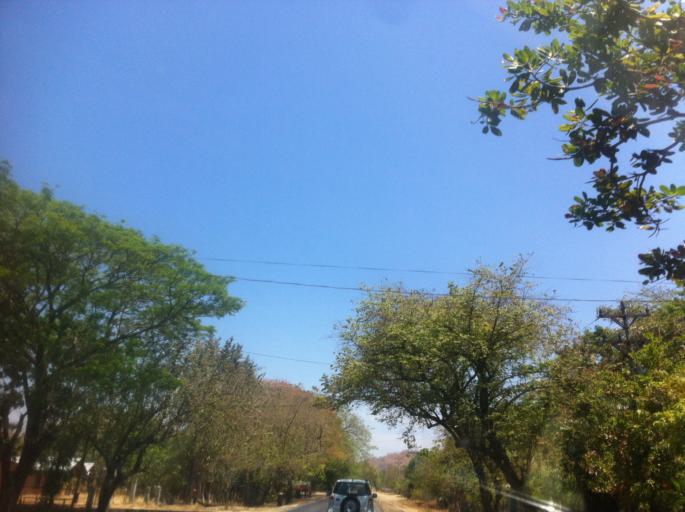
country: CR
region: Guanacaste
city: Belen
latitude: 10.3897
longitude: -85.5866
